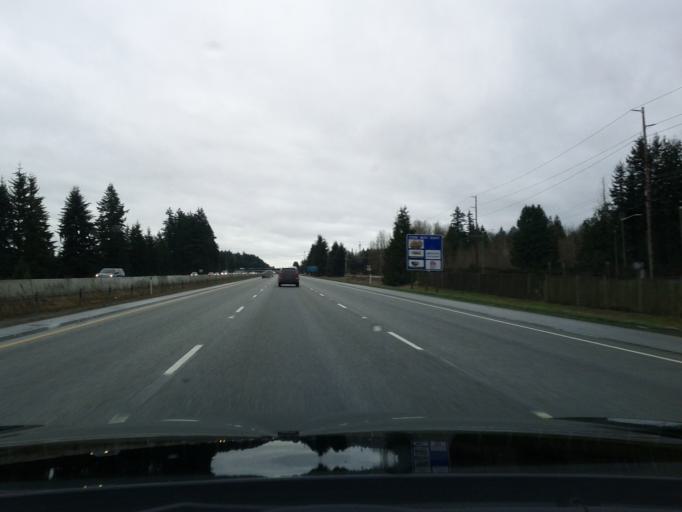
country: US
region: Washington
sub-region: Snohomish County
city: Smokey Point
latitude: 48.1071
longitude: -122.1851
